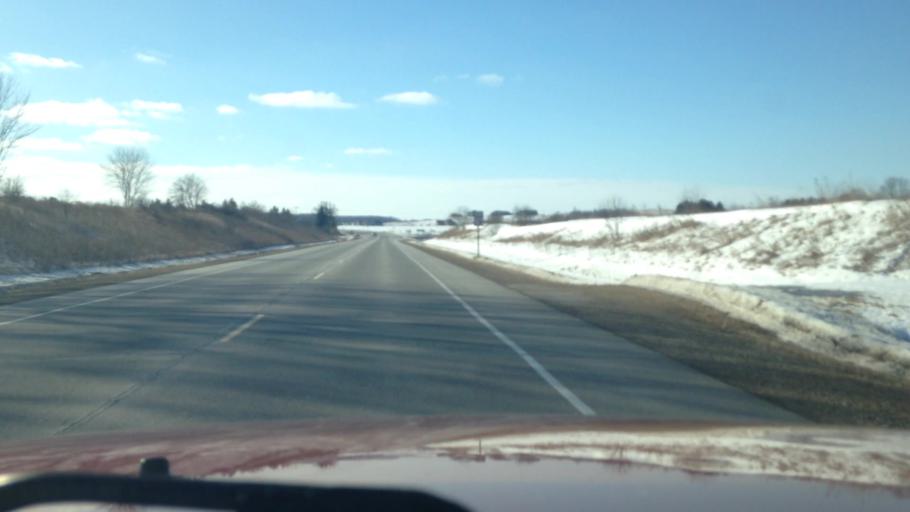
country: US
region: Wisconsin
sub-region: Waukesha County
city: Oconomowoc
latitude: 43.1834
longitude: -88.5088
